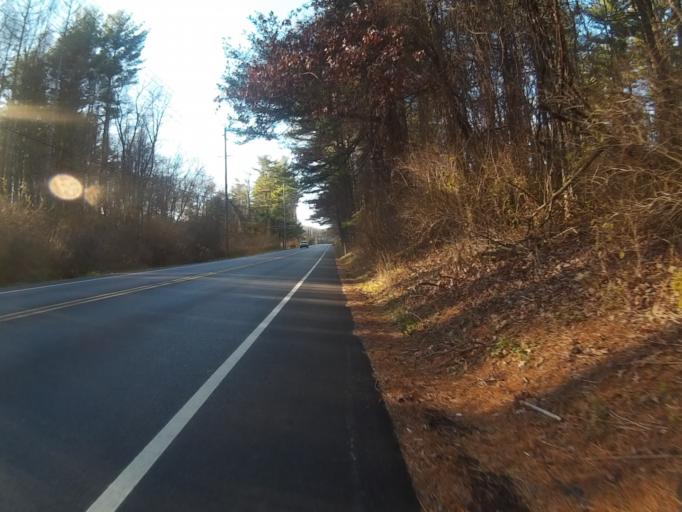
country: US
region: Pennsylvania
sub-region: Centre County
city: State College
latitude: 40.8266
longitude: -77.8719
